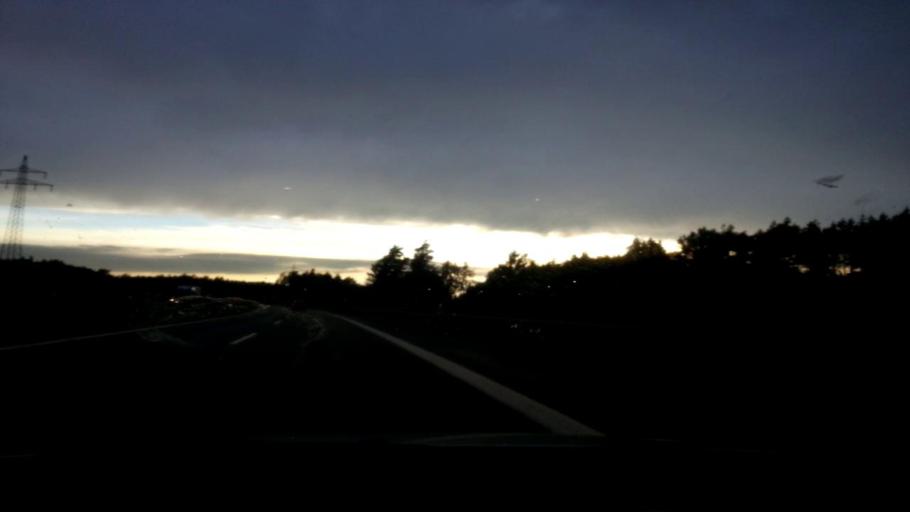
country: DE
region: Bavaria
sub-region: Upper Franconia
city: Stadelhofen
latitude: 50.0105
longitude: 11.2350
